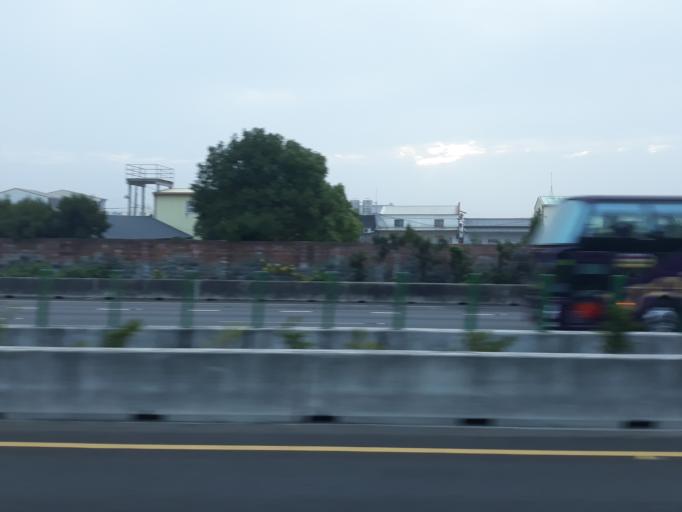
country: TW
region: Taiwan
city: Fengyuan
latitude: 24.3062
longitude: 120.6988
